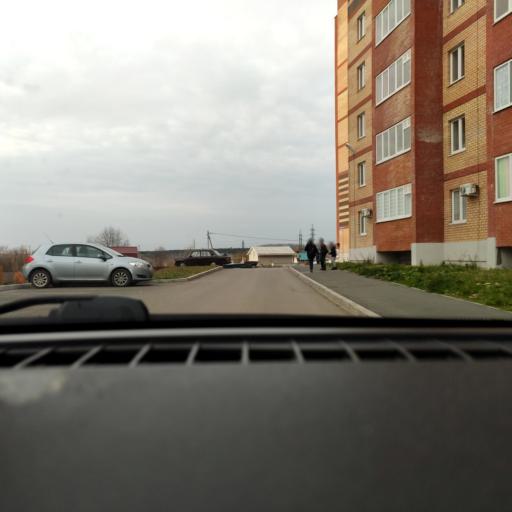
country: RU
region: Perm
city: Froly
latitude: 57.9235
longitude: 56.2735
